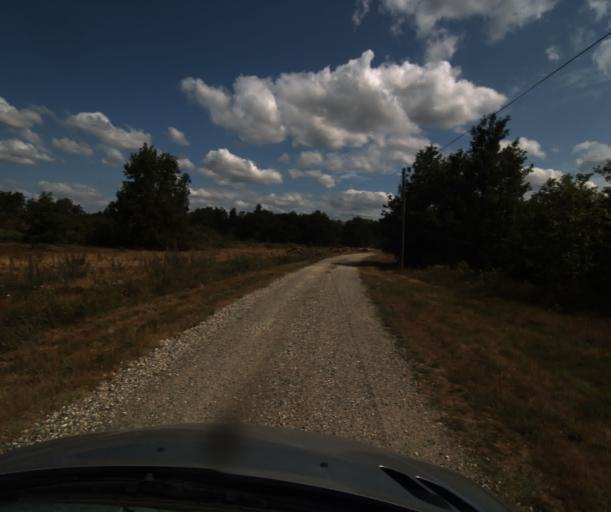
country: FR
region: Midi-Pyrenees
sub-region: Departement du Tarn-et-Garonne
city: Finhan
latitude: 43.9245
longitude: 1.2731
